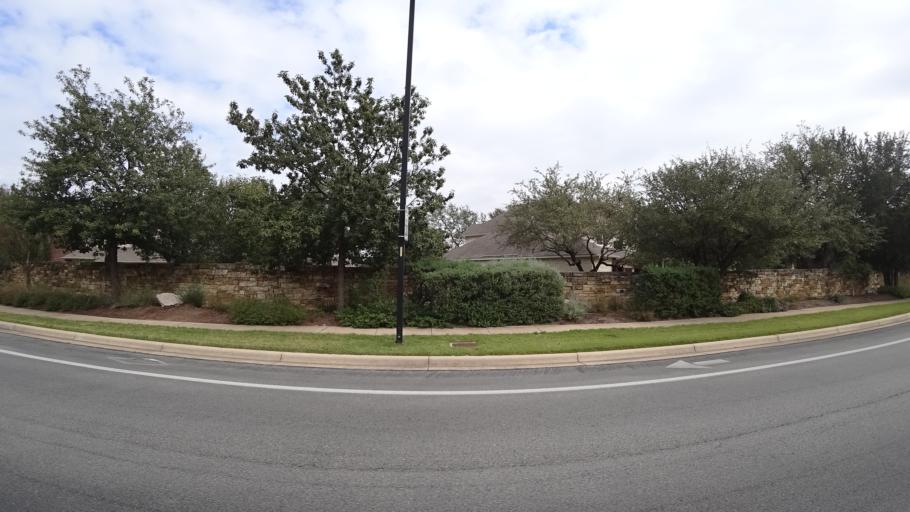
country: US
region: Texas
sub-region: Travis County
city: Shady Hollow
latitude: 30.1884
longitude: -97.9062
